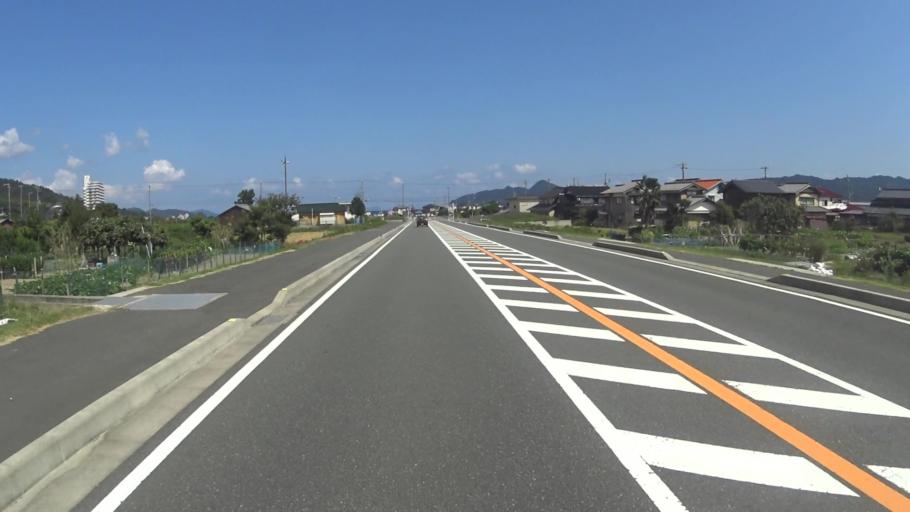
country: JP
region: Kyoto
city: Miyazu
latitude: 35.5833
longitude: 135.2016
